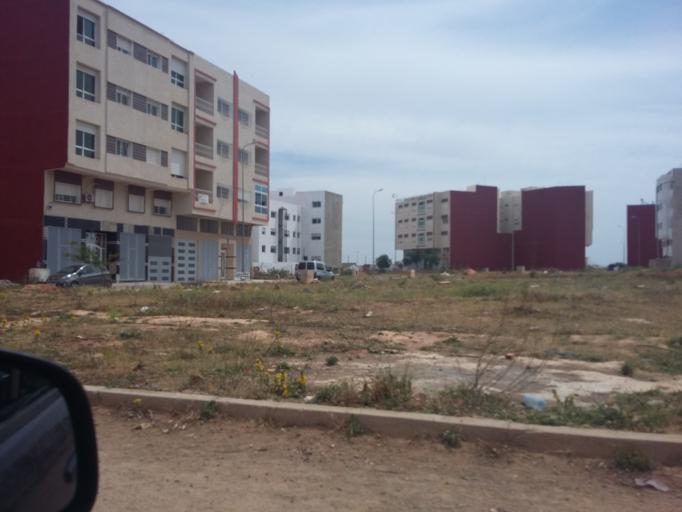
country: MA
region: Fes-Boulemane
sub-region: Fes
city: Fes
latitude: 33.9946
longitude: -5.0055
